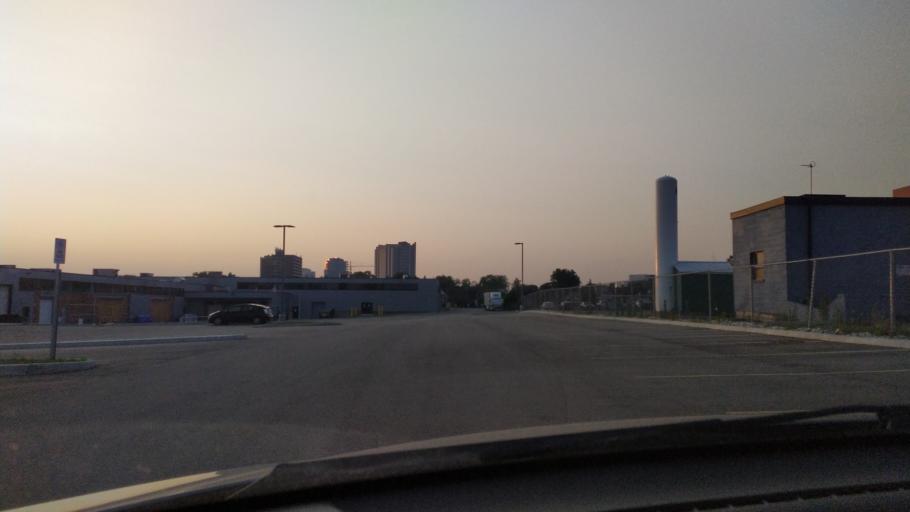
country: CA
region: Ontario
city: Waterloo
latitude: 43.4507
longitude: -80.5118
